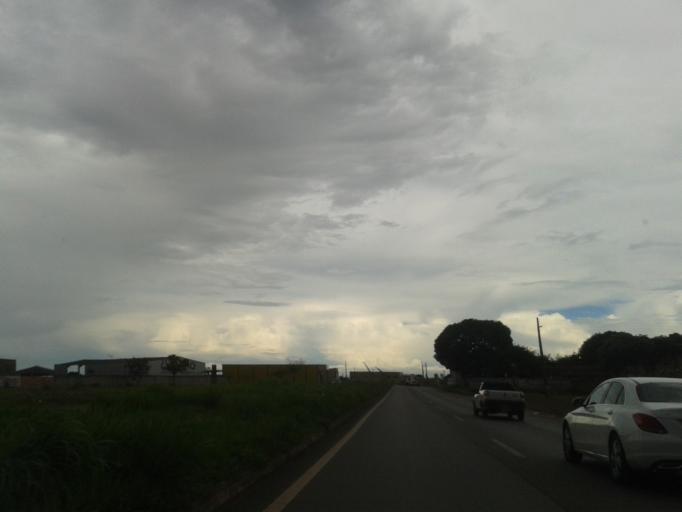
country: BR
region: Goias
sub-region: Aparecida De Goiania
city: Aparecida de Goiania
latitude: -16.7727
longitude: -49.3072
